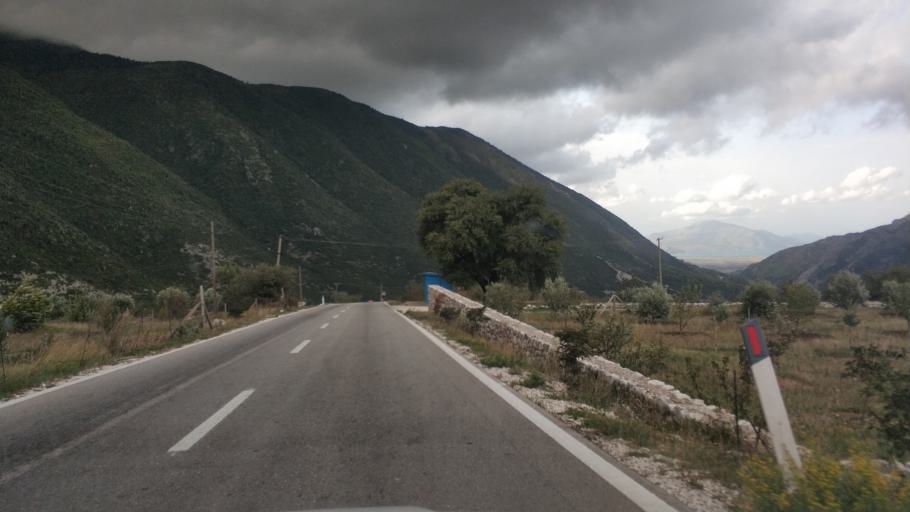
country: AL
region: Vlore
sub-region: Rrethi i Vlores
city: Brataj
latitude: 40.2312
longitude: 19.5676
